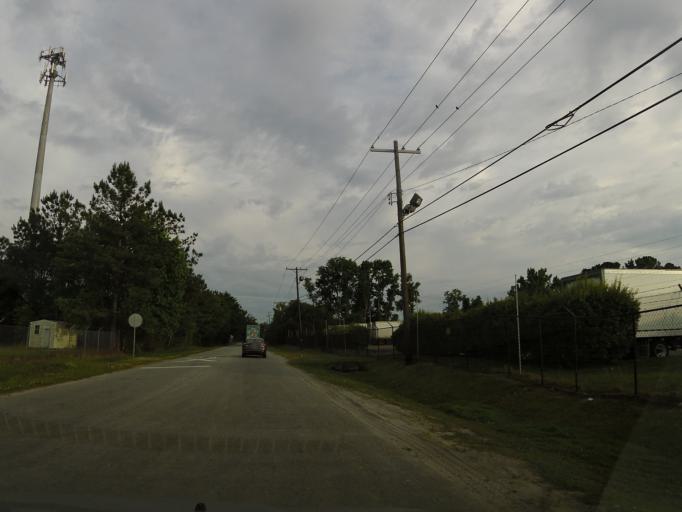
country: US
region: Georgia
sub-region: Chatham County
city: Garden City
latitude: 32.0895
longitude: -81.1993
